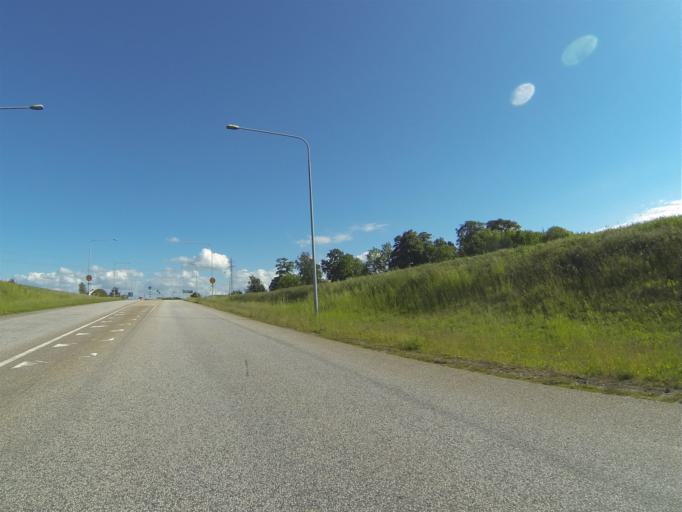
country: SE
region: Skane
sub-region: Burlovs Kommun
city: Arloev
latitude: 55.6345
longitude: 13.0954
